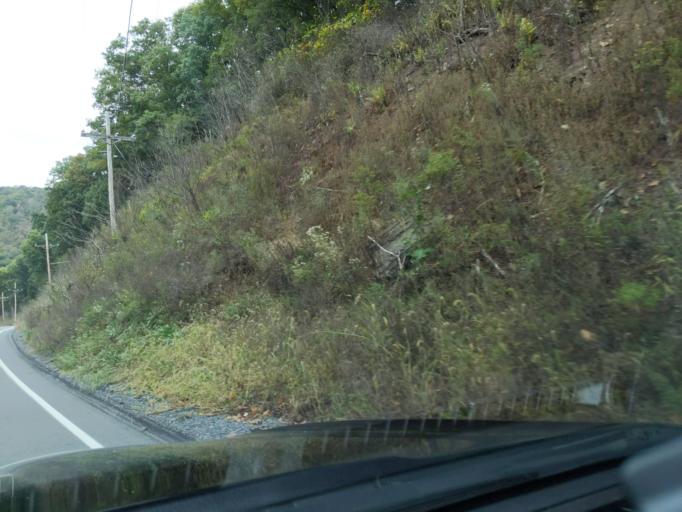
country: US
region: Pennsylvania
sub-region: Blair County
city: Altoona
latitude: 40.4962
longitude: -78.4670
